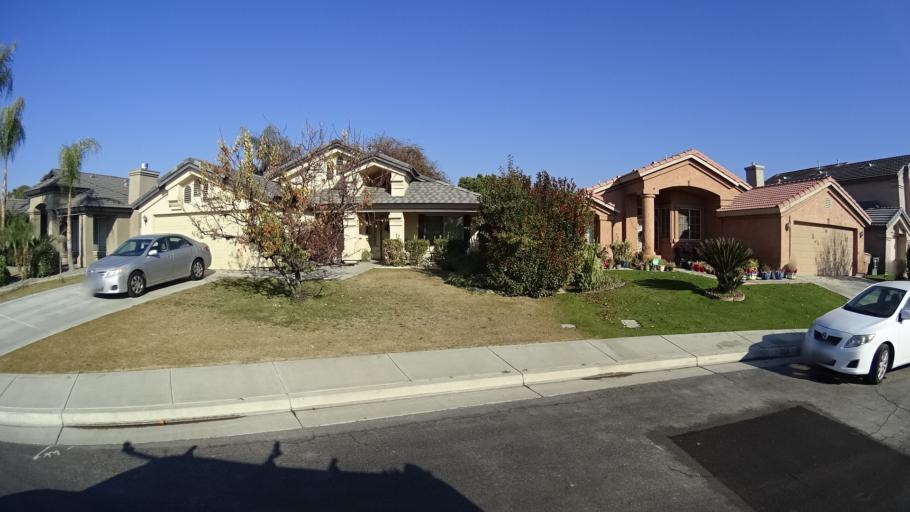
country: US
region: California
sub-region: Kern County
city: Greenacres
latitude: 35.3090
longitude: -119.1165
